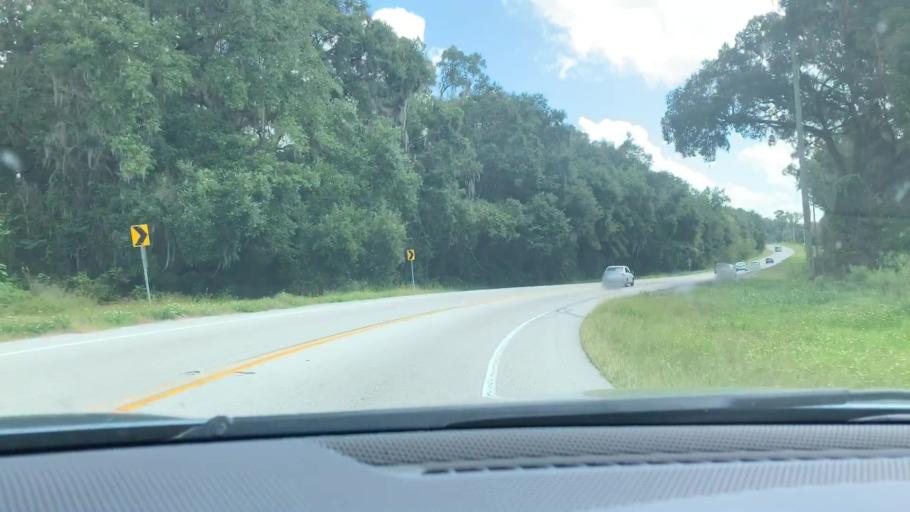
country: US
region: Florida
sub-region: Marion County
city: Ocala
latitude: 29.2667
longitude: -82.1733
